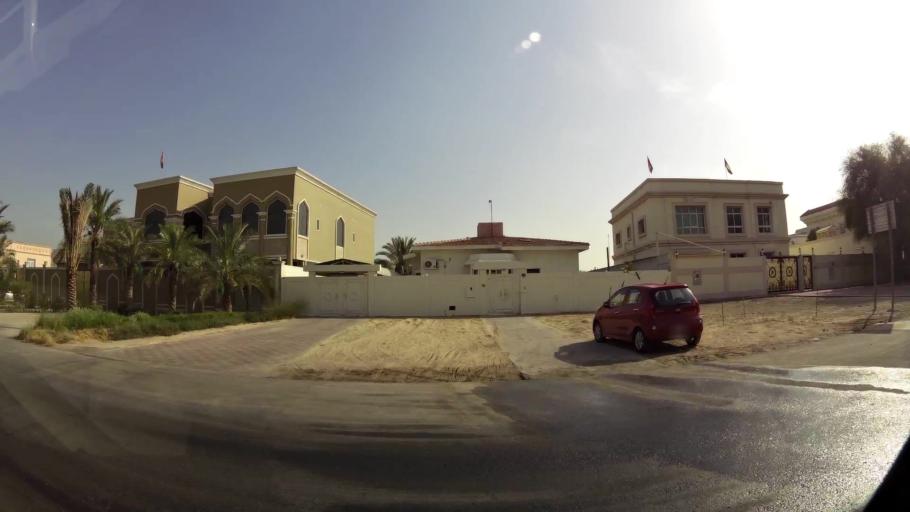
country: AE
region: Ash Shariqah
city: Sharjah
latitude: 25.2162
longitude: 55.3930
